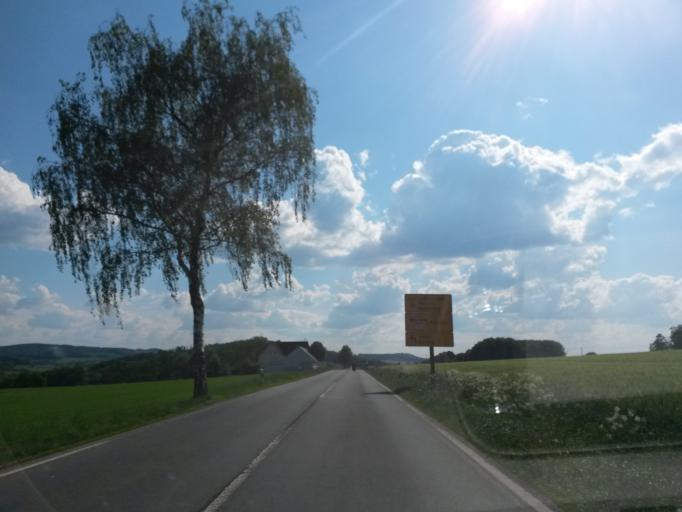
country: DE
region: North Rhine-Westphalia
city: Balve
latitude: 51.2966
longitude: 7.8486
